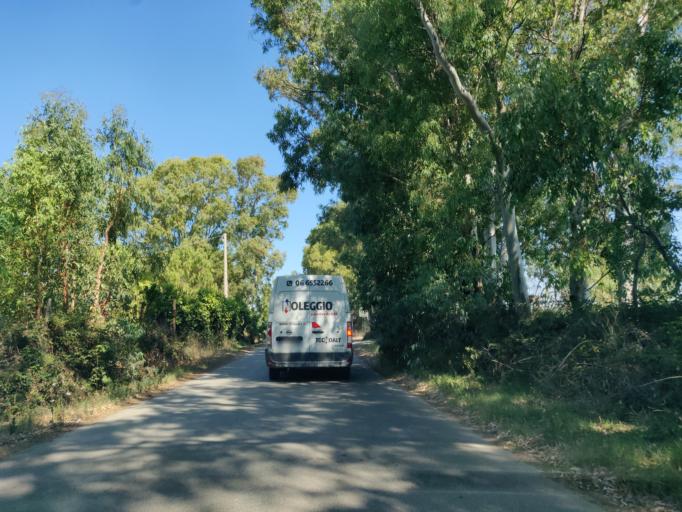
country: IT
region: Latium
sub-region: Citta metropolitana di Roma Capitale
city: Aurelia
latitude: 42.1653
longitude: 11.7421
